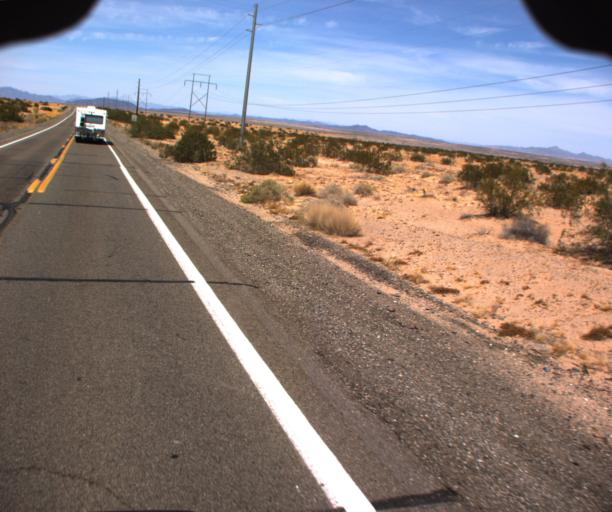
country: US
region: Arizona
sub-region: La Paz County
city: Parker
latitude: 33.9506
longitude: -114.2169
